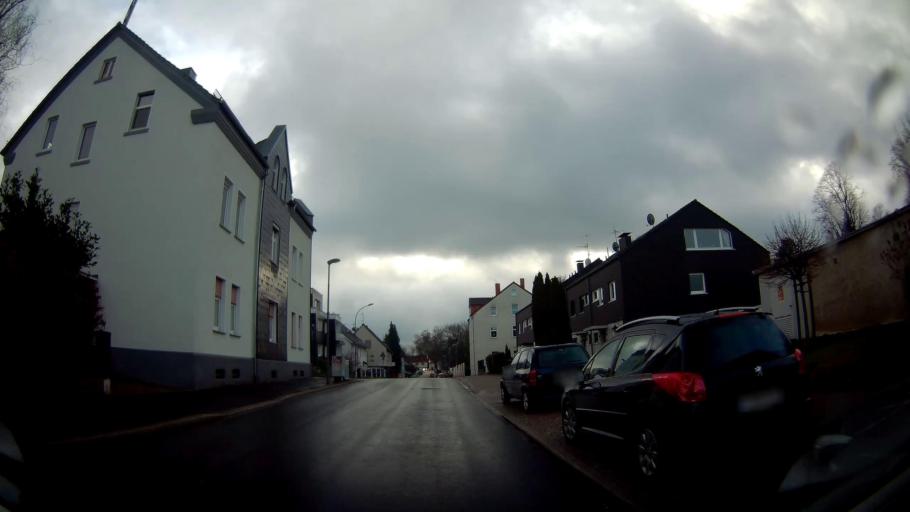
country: DE
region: North Rhine-Westphalia
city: Castrop-Rauxel
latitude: 51.5032
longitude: 7.2838
